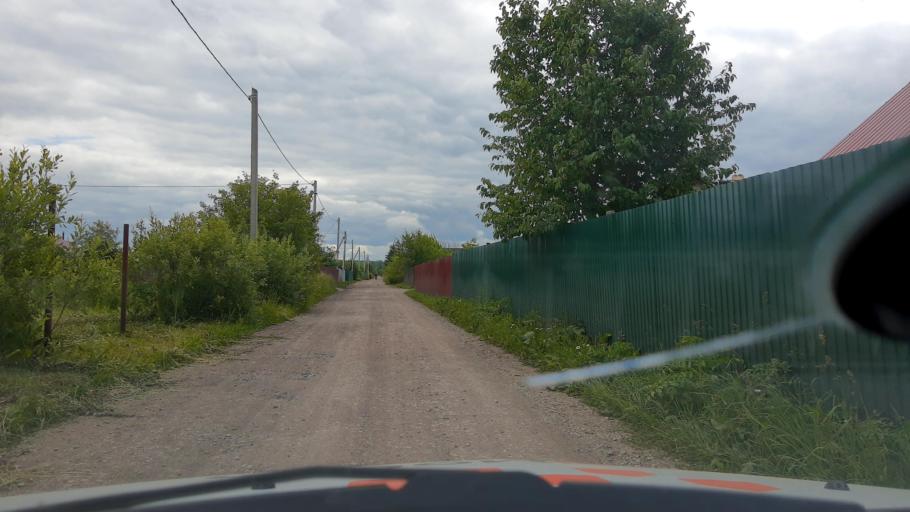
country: RU
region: Bashkortostan
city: Kabakovo
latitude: 54.7260
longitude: 56.2020
